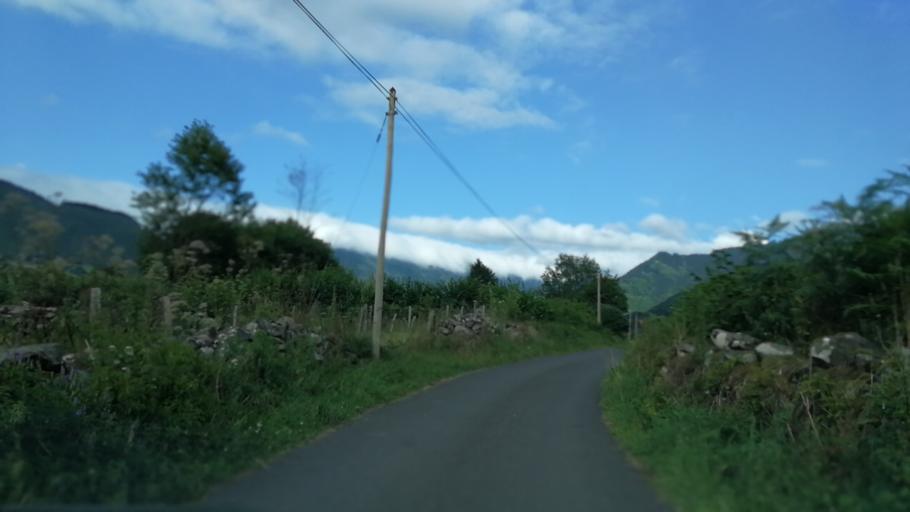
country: FR
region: Aquitaine
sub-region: Departement des Pyrenees-Atlantiques
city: Arette
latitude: 42.9220
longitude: -0.6527
